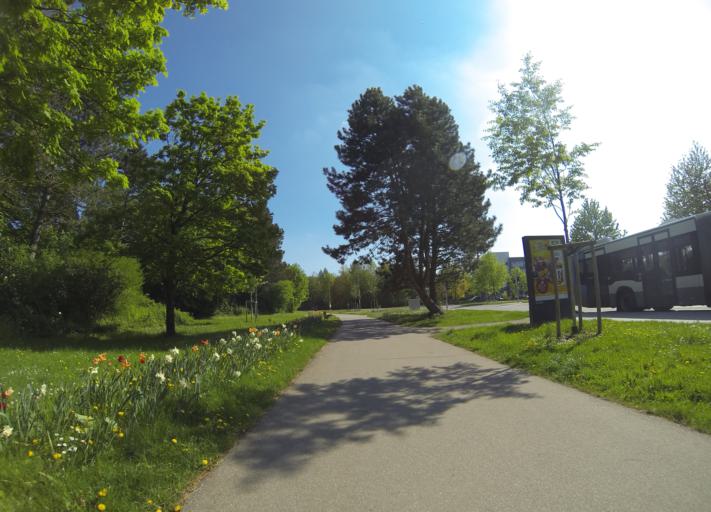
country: DE
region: Baden-Wuerttemberg
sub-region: Tuebingen Region
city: Staig
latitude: 48.3482
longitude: 9.9686
